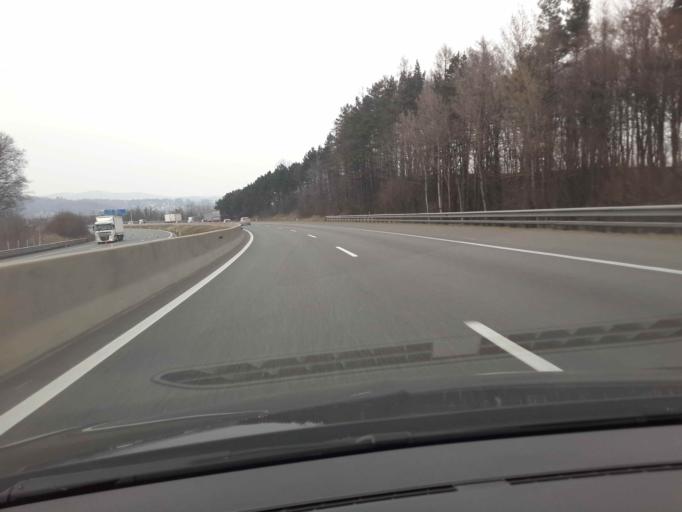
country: AT
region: Lower Austria
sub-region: Politischer Bezirk Sankt Polten
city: Eichgraben
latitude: 48.1447
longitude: 15.9838
